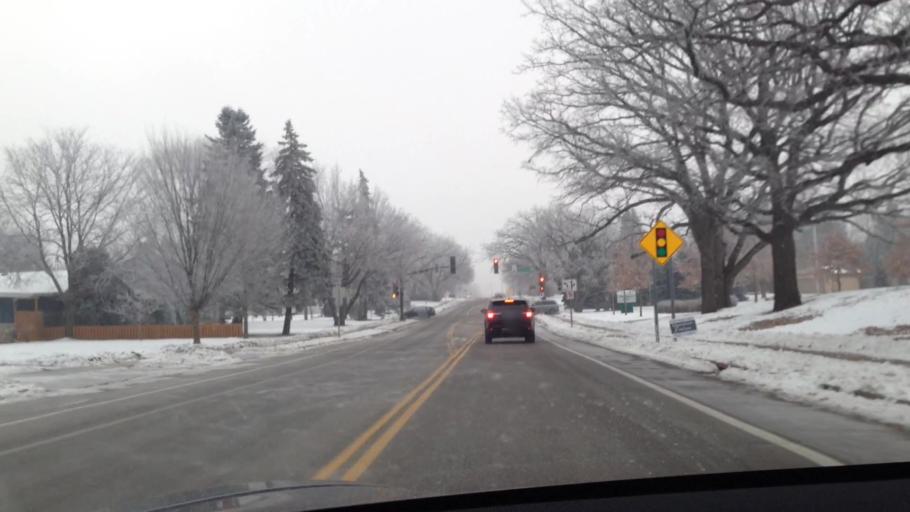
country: US
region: Minnesota
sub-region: Hennepin County
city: Edina
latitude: 44.8764
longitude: -93.3376
